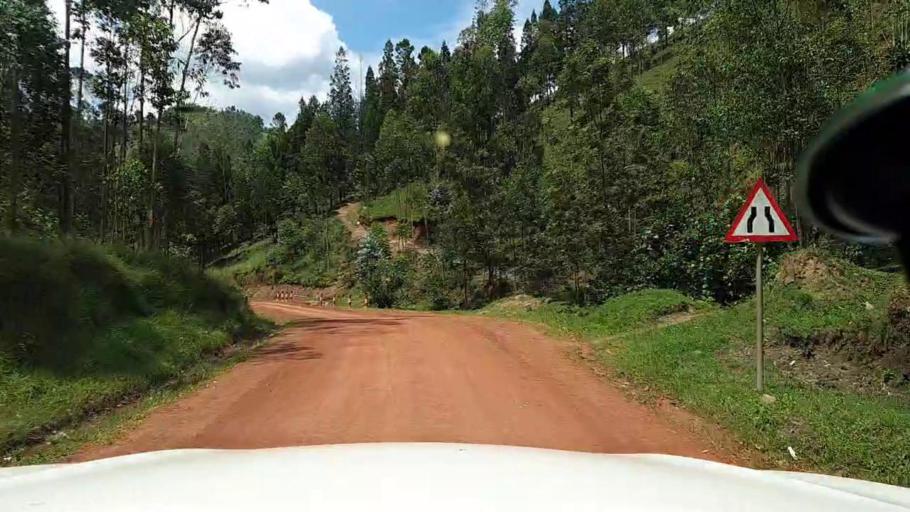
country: RW
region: Northern Province
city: Byumba
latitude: -1.7001
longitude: 29.8334
